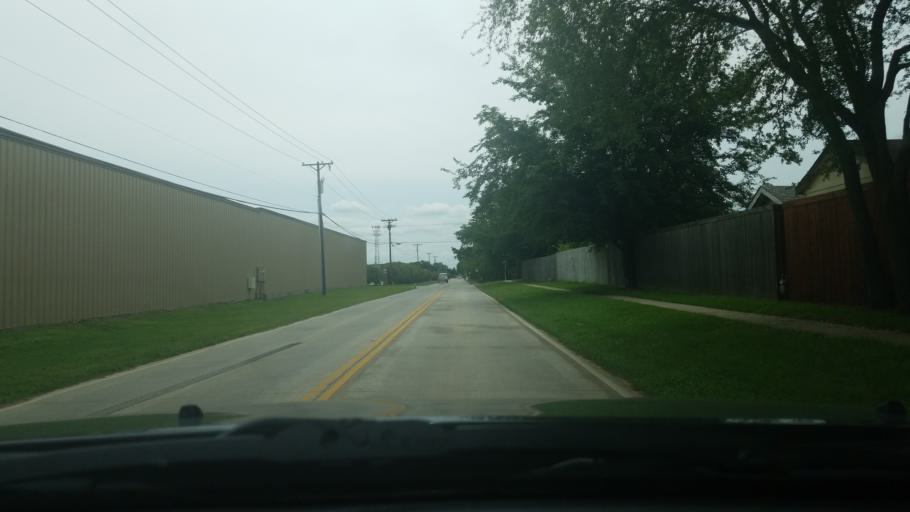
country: US
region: Texas
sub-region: Denton County
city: Lake Dallas
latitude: 33.1096
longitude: -97.0140
